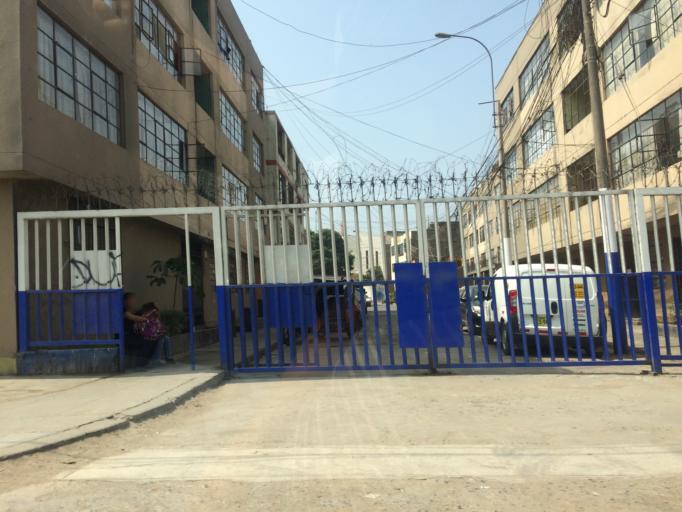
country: PE
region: Lima
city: Lima
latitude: -12.0279
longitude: -77.0410
